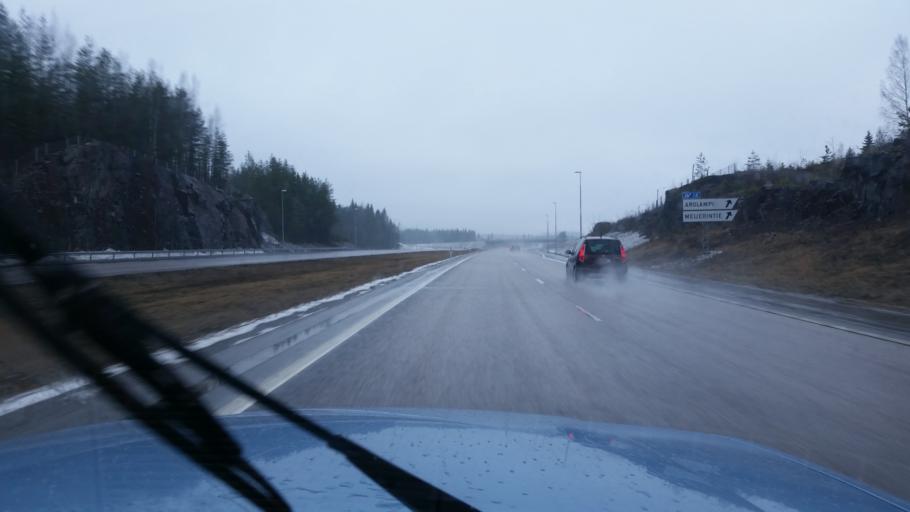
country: FI
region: Haeme
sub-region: Riihimaeki
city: Riihimaeki
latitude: 60.6826
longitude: 24.7565
